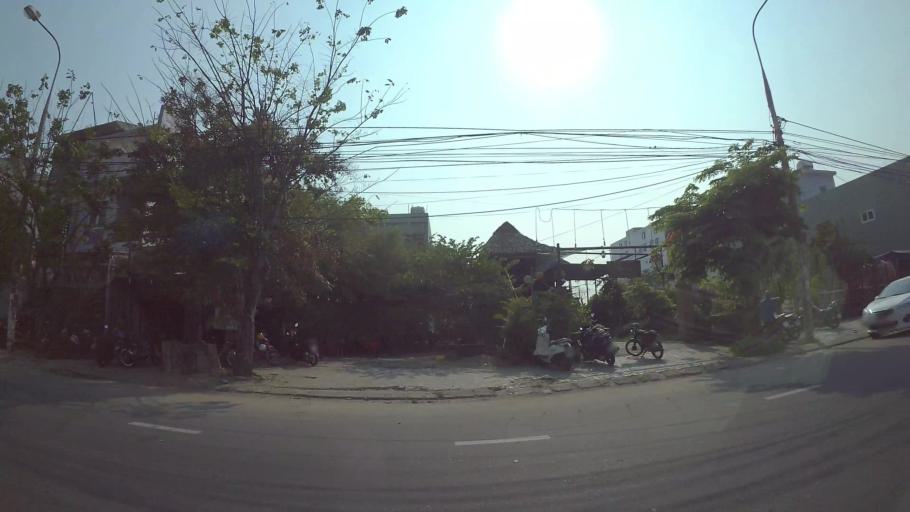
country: VN
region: Da Nang
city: Cam Le
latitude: 16.0158
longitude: 108.1994
